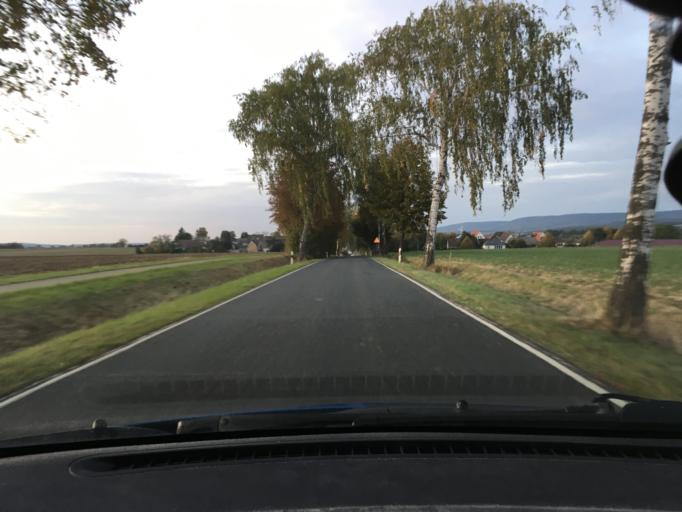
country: DE
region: Lower Saxony
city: Messenkamp
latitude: 52.2151
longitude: 9.3972
